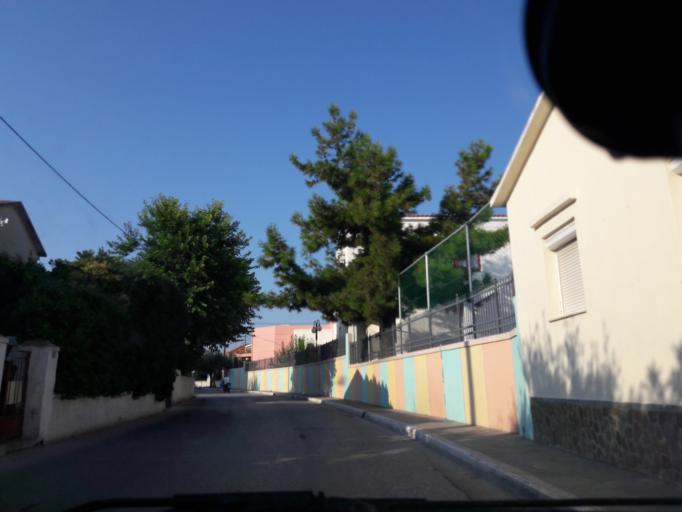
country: GR
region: North Aegean
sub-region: Nomos Lesvou
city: Myrina
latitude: 39.8743
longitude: 25.0633
